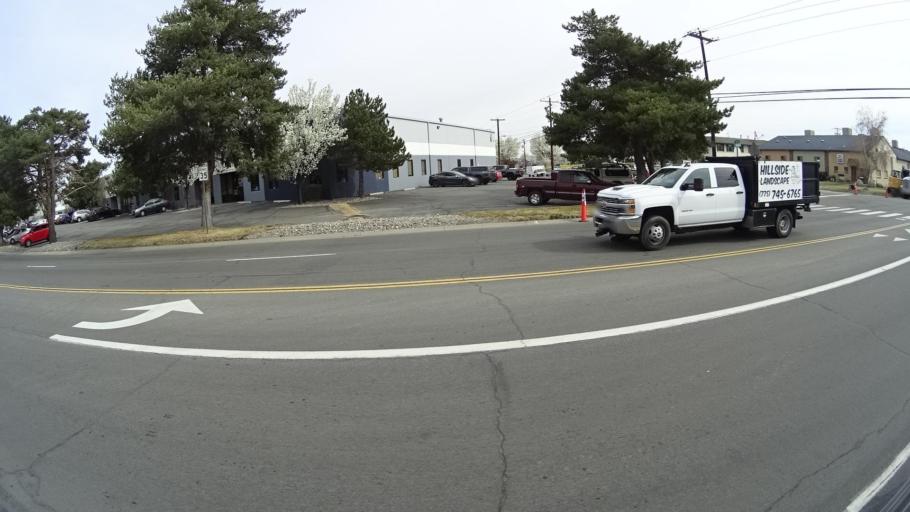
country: US
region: Nevada
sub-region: Washoe County
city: Sparks
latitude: 39.5215
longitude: -119.7545
